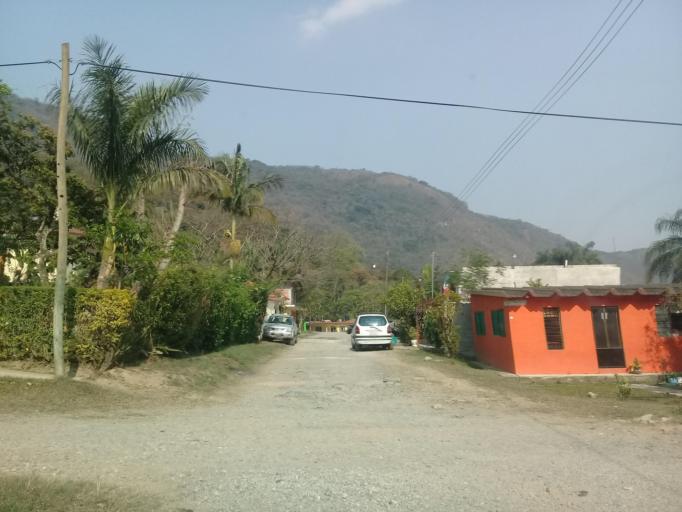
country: MX
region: Veracruz
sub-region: Ixtaczoquitlan
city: Campo Chico
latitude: 18.8387
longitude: -97.0300
